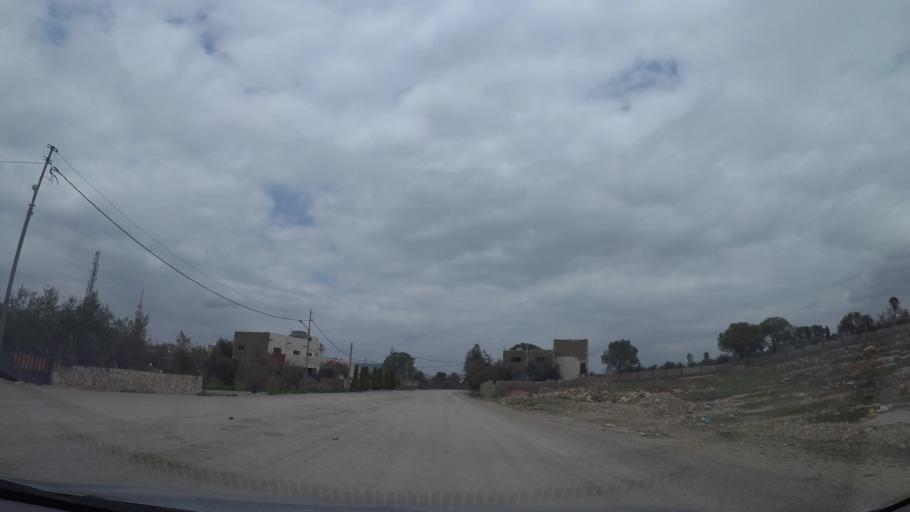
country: JO
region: Amman
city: Al Jubayhah
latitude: 32.0569
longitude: 35.8399
